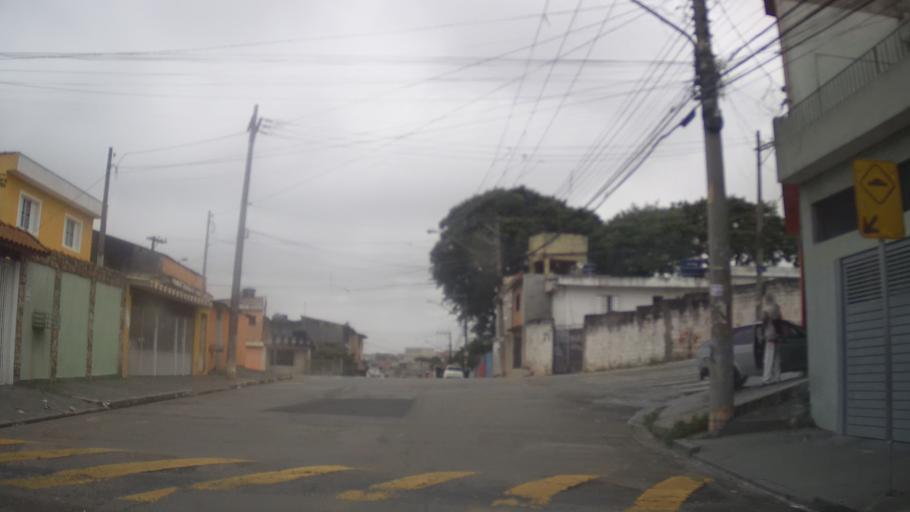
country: BR
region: Sao Paulo
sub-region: Guarulhos
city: Guarulhos
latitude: -23.4374
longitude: -46.5140
